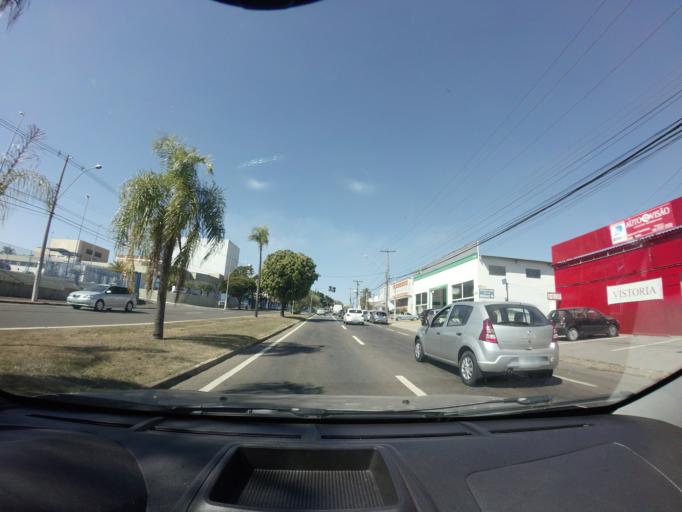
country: BR
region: Sao Paulo
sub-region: Piracicaba
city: Piracicaba
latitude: -22.7294
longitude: -47.6159
